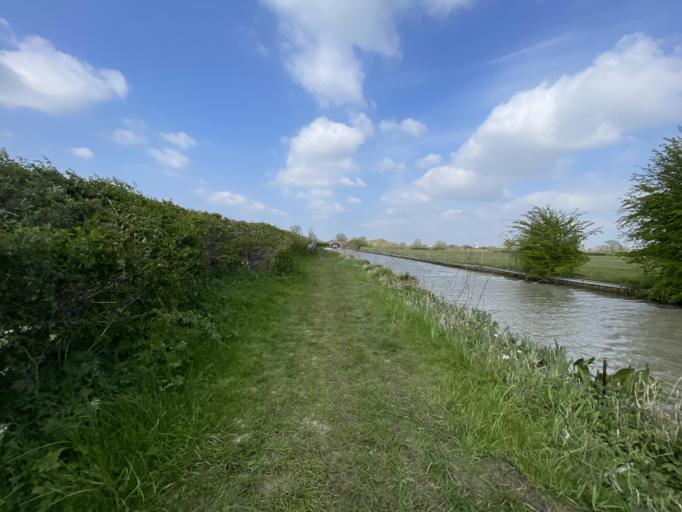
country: GB
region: England
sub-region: Warwickshire
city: Rugby
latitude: 52.3457
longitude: -1.2086
